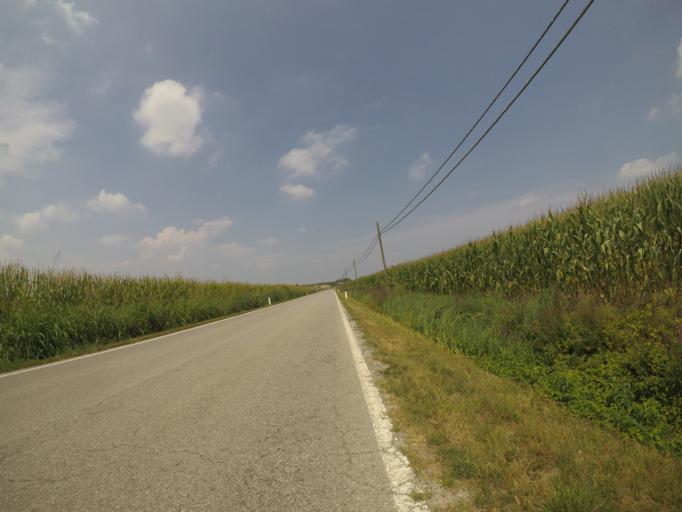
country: IT
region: Friuli Venezia Giulia
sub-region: Provincia di Udine
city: Pocenia
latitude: 45.8393
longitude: 13.0778
